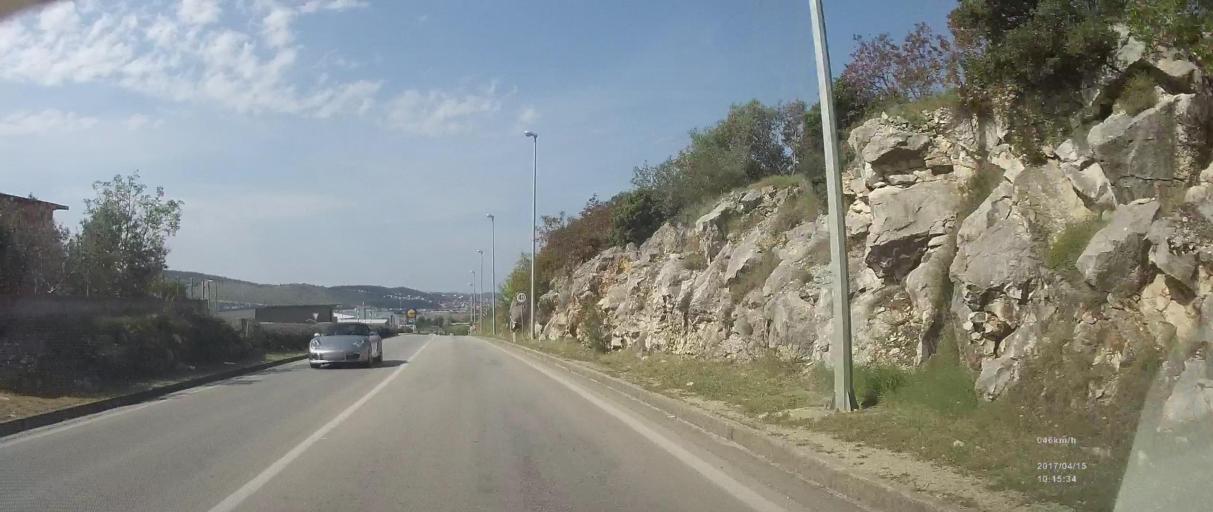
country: HR
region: Splitsko-Dalmatinska
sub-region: Grad Trogir
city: Trogir
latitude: 43.5348
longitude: 16.2837
